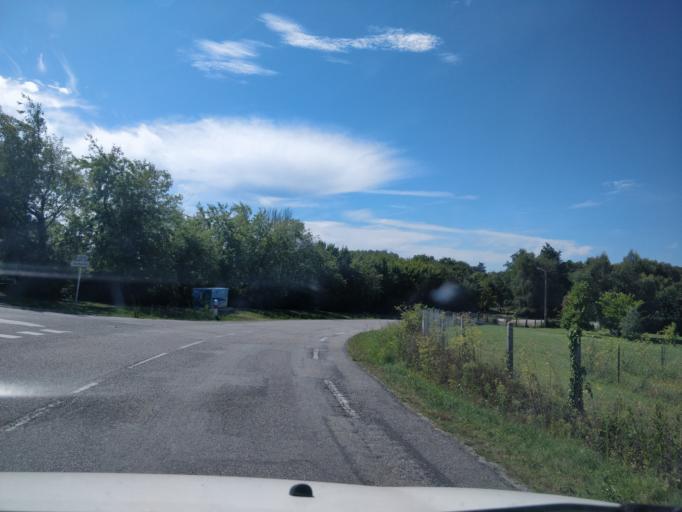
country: FR
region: Brittany
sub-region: Departement du Morbihan
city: Saint-Philibert
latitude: 47.5802
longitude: -2.9979
